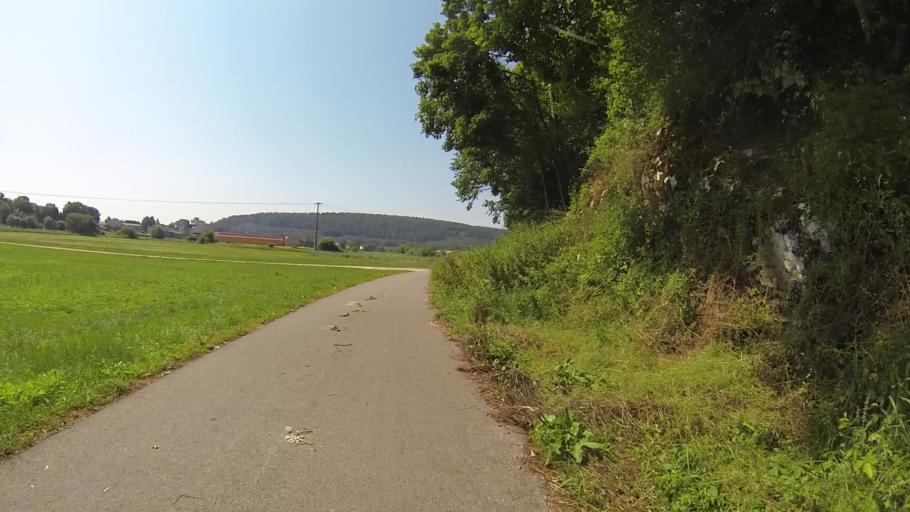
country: DE
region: Baden-Wuerttemberg
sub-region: Regierungsbezirk Stuttgart
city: Konigsbronn
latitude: 48.7257
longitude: 10.1542
